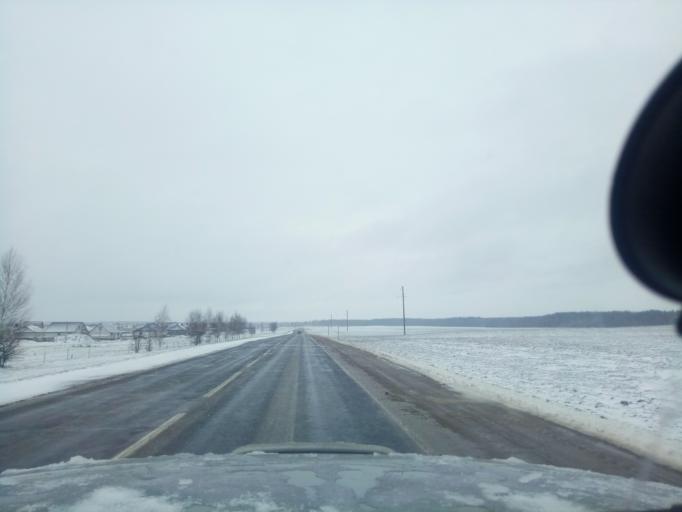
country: BY
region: Minsk
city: Nyasvizh
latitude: 53.2243
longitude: 26.6457
